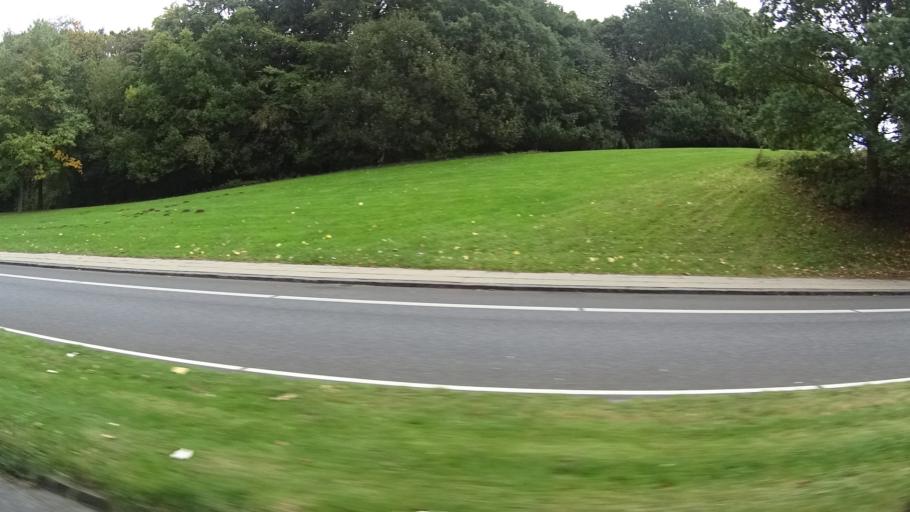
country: DK
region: South Denmark
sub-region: Vejle Kommune
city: Vejle
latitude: 55.6903
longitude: 9.5227
